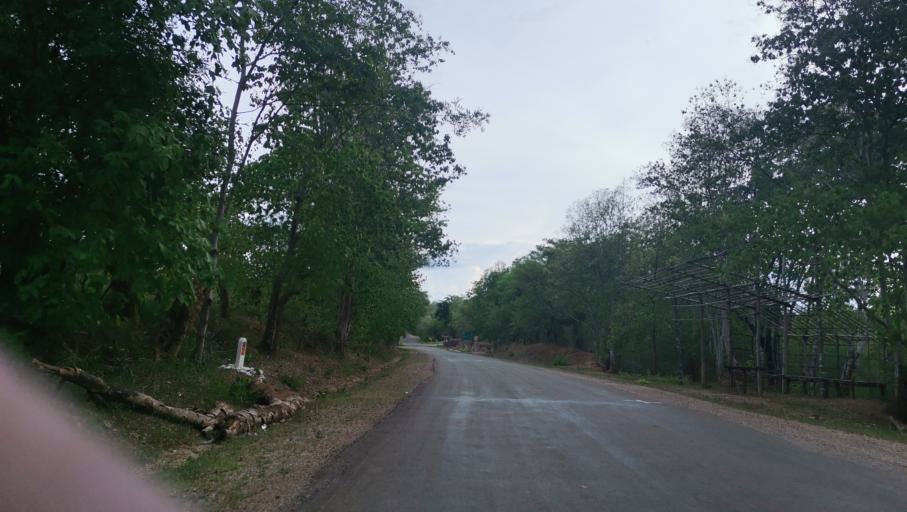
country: MM
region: Magway
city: Minbu
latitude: 20.0882
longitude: 94.5799
